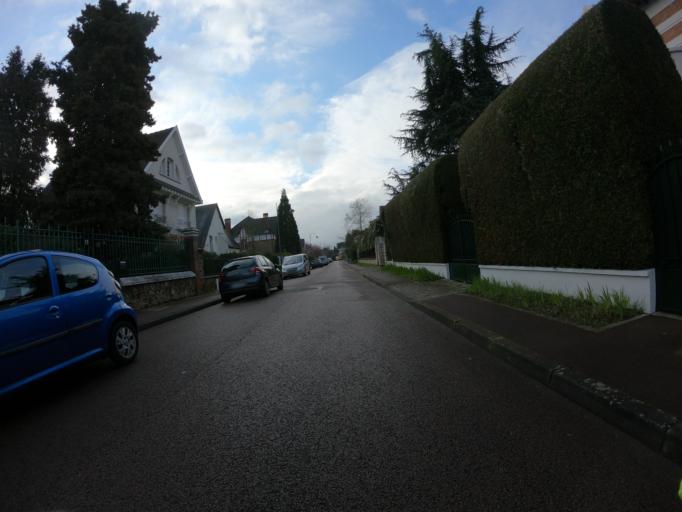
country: FR
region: Ile-de-France
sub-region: Departement des Hauts-de-Seine
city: Bourg-la-Reine
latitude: 48.7738
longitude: 2.3070
